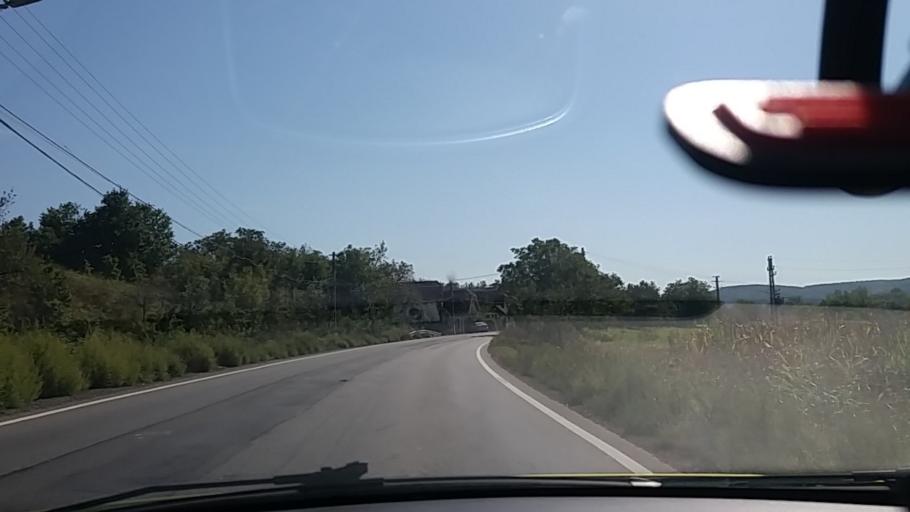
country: RO
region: Arad
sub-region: Comuna Conop
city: Conop
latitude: 46.1080
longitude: 21.8658
